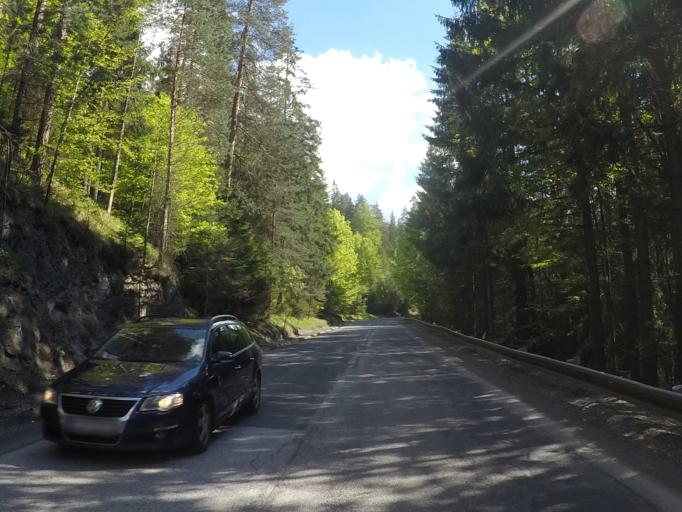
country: SK
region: Kosicky
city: Dobsina
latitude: 48.9141
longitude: 20.2609
